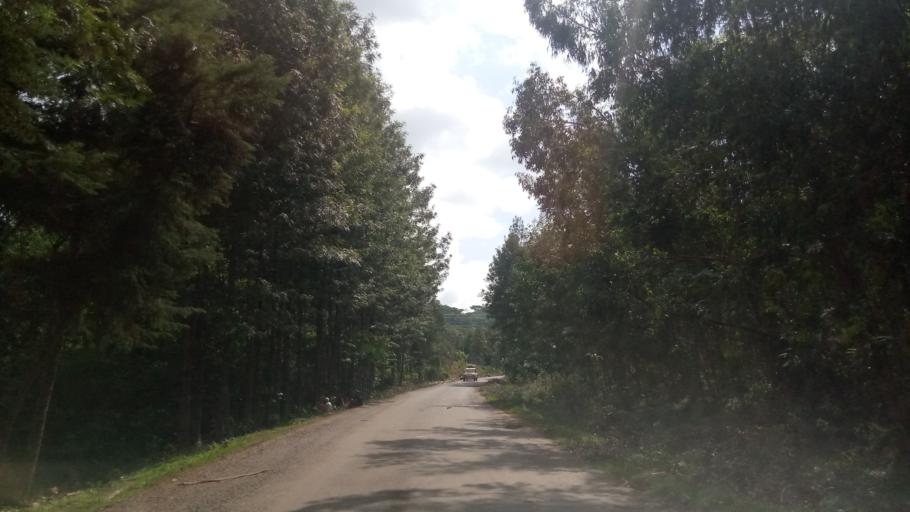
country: ET
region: Oromiya
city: Agaro
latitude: 7.9204
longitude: 36.5230
